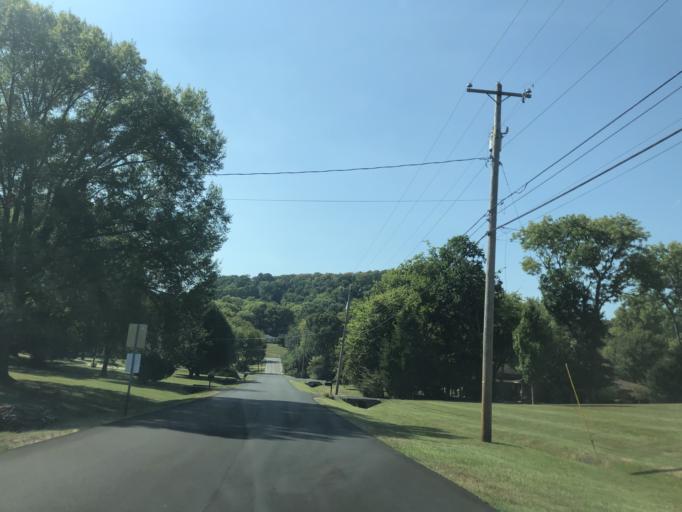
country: US
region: Tennessee
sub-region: Davidson County
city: Forest Hills
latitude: 36.0834
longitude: -86.8174
